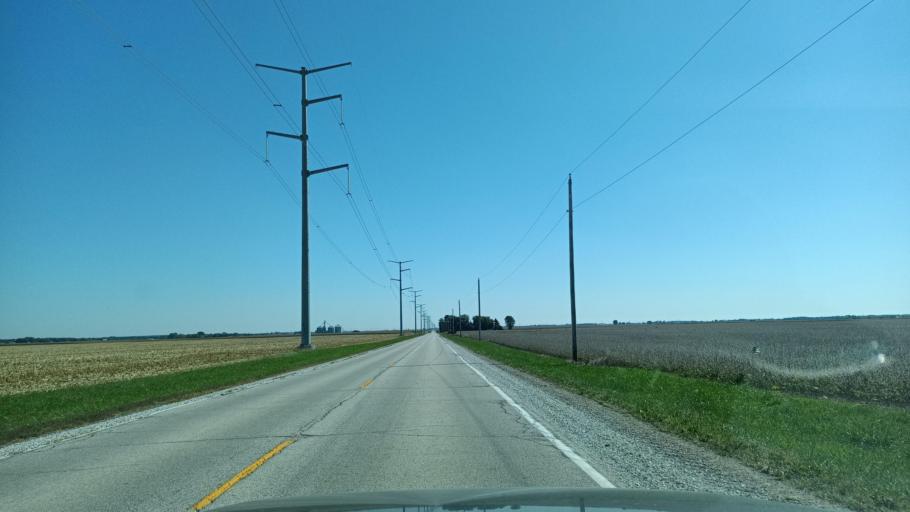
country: US
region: Illinois
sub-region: Peoria County
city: Elmwood
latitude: 40.9024
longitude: -90.0414
